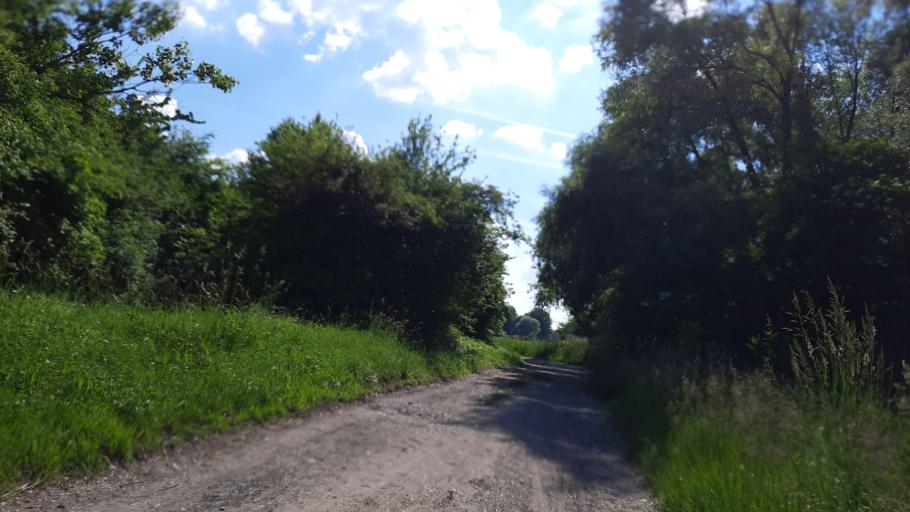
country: DE
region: Bavaria
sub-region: Upper Bavaria
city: Aschheim
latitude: 48.1734
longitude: 11.6821
